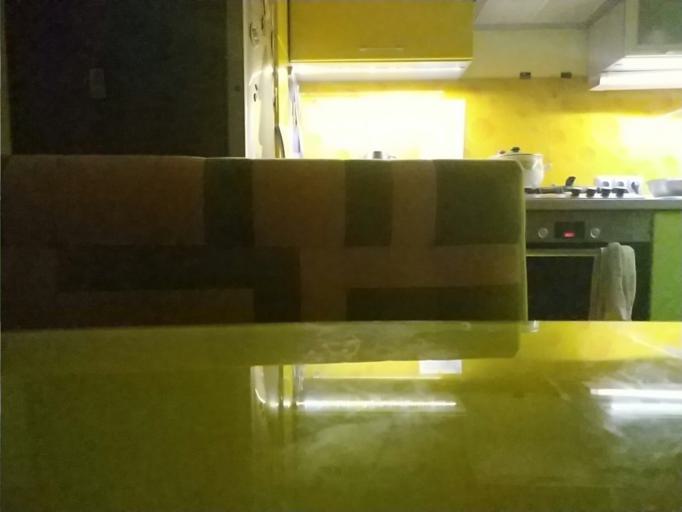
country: RU
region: Republic of Karelia
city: Pyaozerskiy
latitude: 65.6073
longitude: 30.5611
